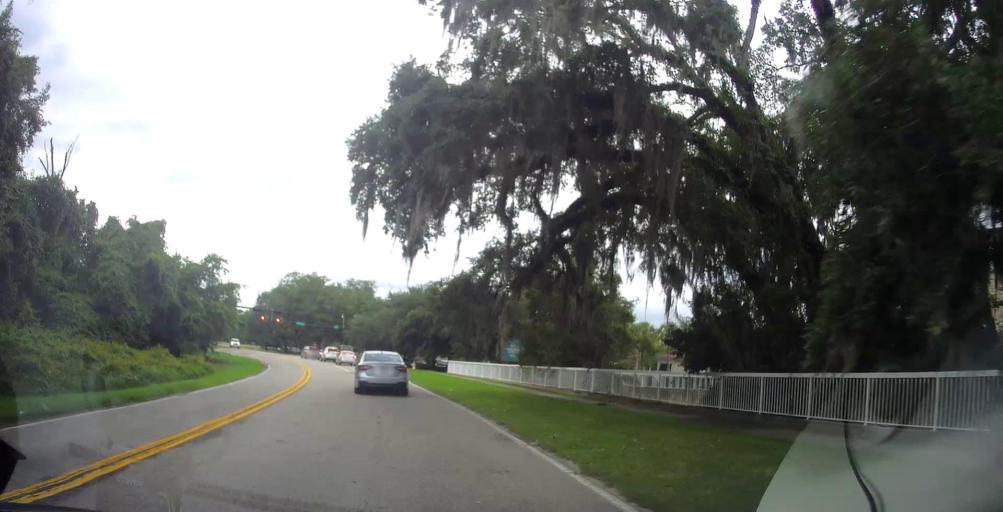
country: US
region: Florida
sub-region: Alachua County
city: Gainesville
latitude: 29.6212
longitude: -82.3863
